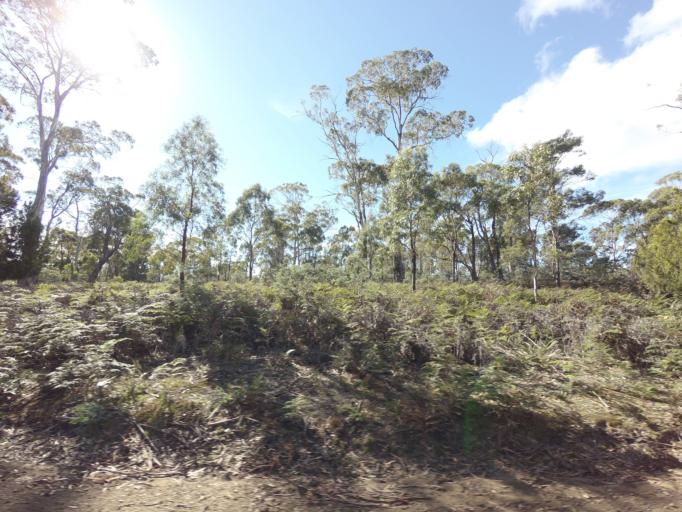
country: AU
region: Tasmania
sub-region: Clarence
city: Sandford
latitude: -42.9623
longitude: 147.7031
